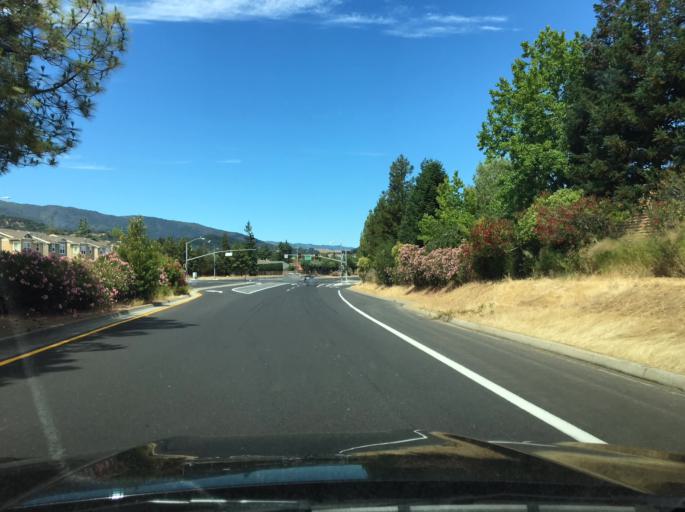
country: US
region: California
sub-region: Santa Clara County
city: Seven Trees
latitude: 37.2042
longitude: -121.8386
